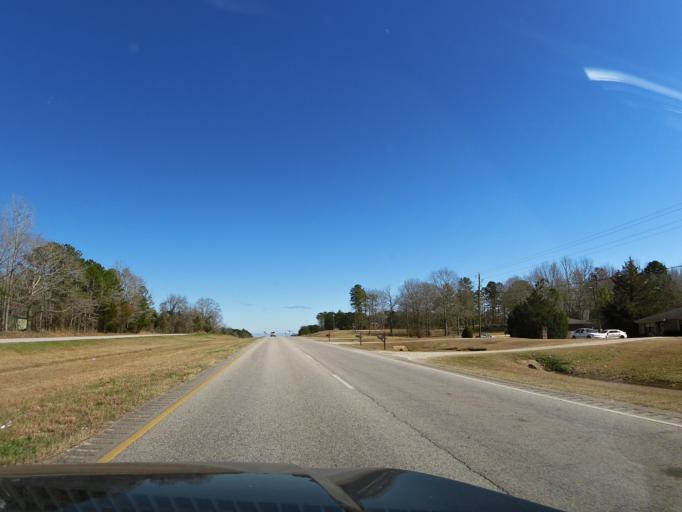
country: US
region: Alabama
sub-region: Bullock County
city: Union Springs
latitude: 32.1461
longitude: -85.6650
